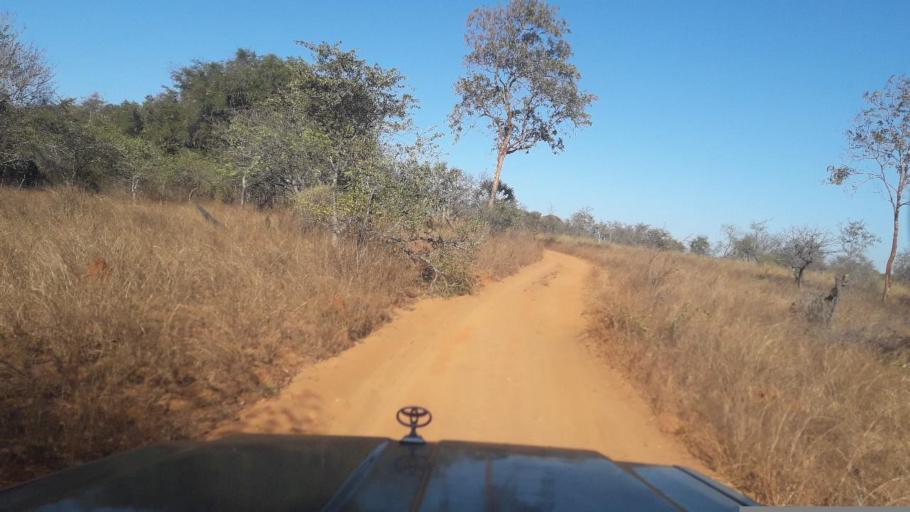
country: MG
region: Boeny
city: Sitampiky
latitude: -16.4152
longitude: 45.6070
